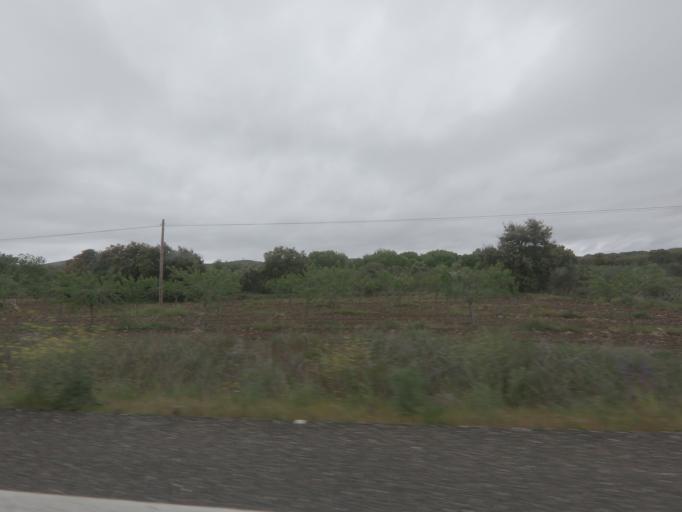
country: ES
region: Extremadura
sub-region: Provincia de Badajoz
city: La Roca de la Sierra
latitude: 39.1194
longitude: -6.6771
